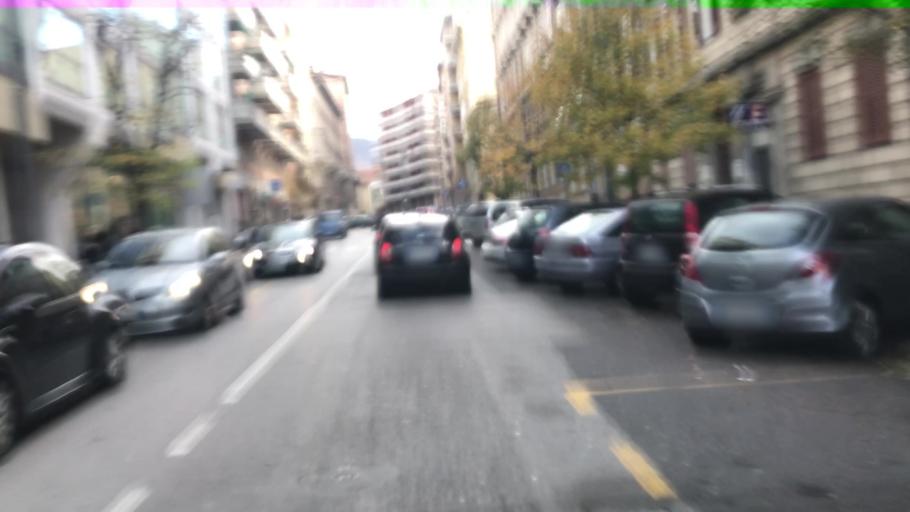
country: IT
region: Friuli Venezia Giulia
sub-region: Provincia di Trieste
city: Trieste
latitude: 45.6565
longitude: 13.7851
